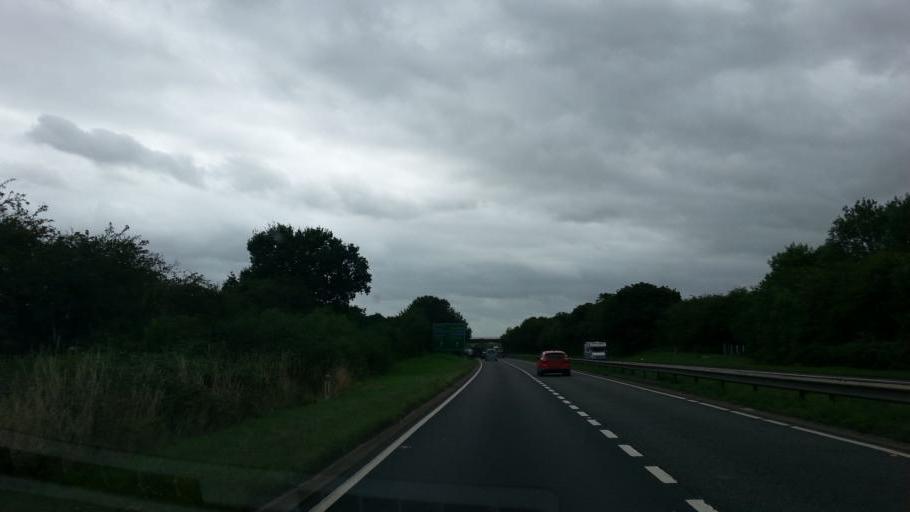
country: GB
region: England
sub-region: Warwickshire
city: Warwick
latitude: 52.2774
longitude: -1.6129
